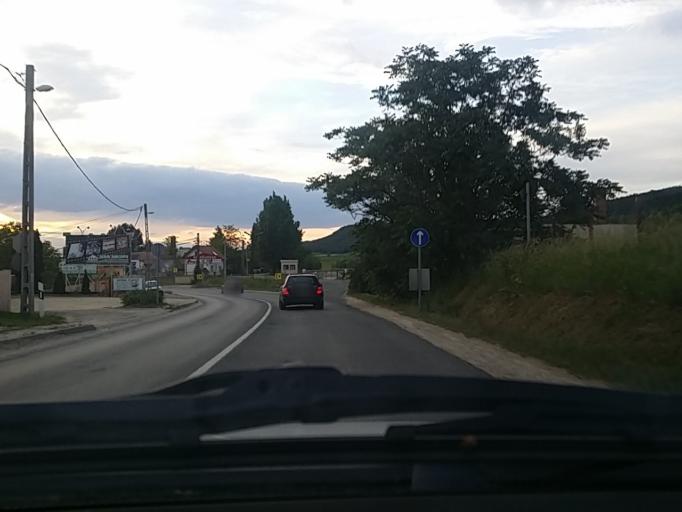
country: HU
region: Pest
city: Pilisborosjeno
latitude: 47.5957
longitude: 18.9788
